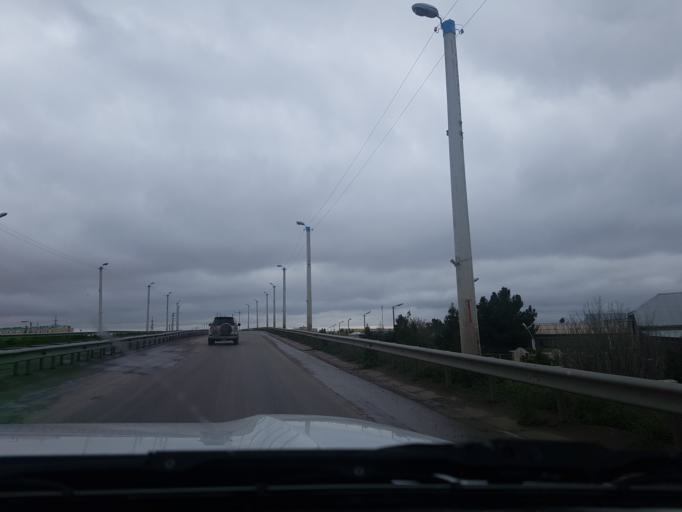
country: TM
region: Mary
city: Mary
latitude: 37.5898
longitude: 61.8834
